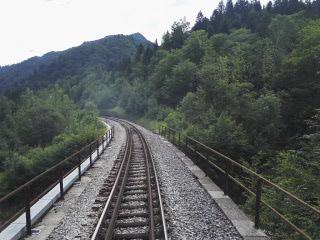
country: SI
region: Cerkno
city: Cerkno
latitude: 46.1706
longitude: 13.9095
